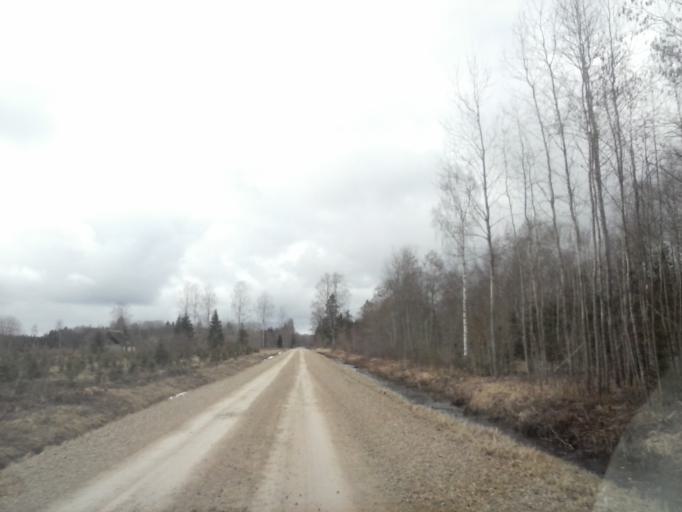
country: EE
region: Jogevamaa
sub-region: Mustvee linn
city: Mustvee
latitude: 59.0949
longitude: 26.8337
